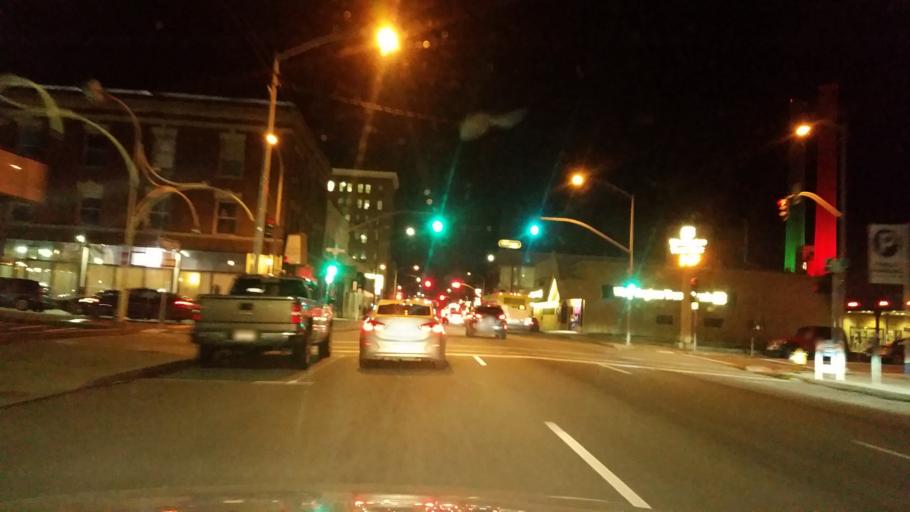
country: US
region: Washington
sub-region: Spokane County
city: Spokane
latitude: 47.6545
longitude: -117.4216
